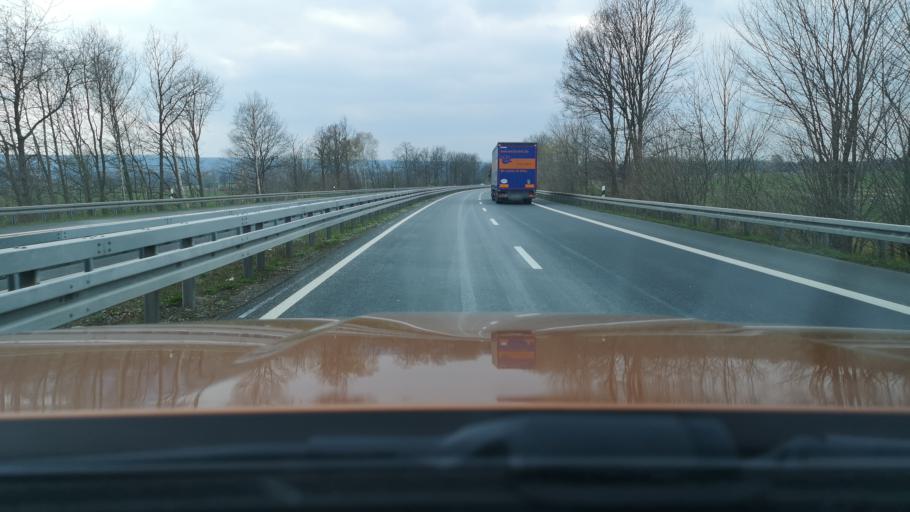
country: DE
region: Lower Saxony
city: Stadthagen
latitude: 52.3164
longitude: 9.2241
